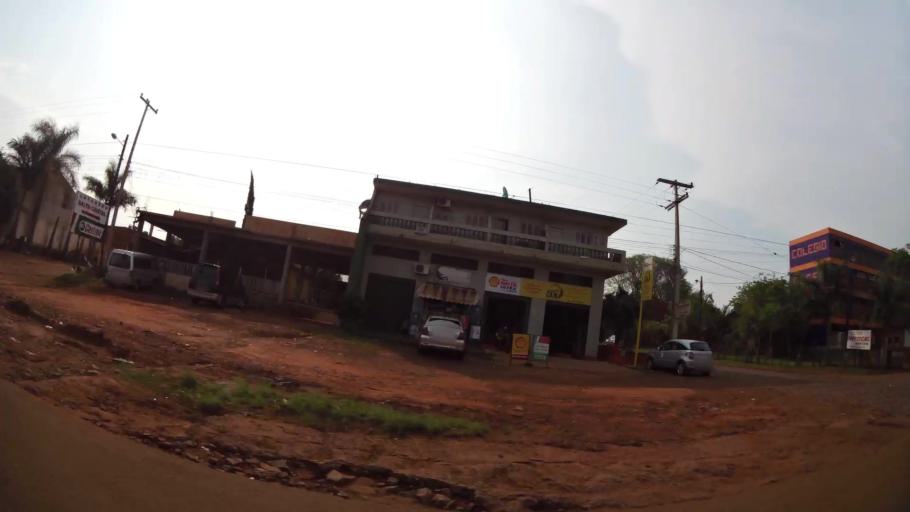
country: PY
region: Alto Parana
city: Ciudad del Este
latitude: -25.4885
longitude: -54.6632
